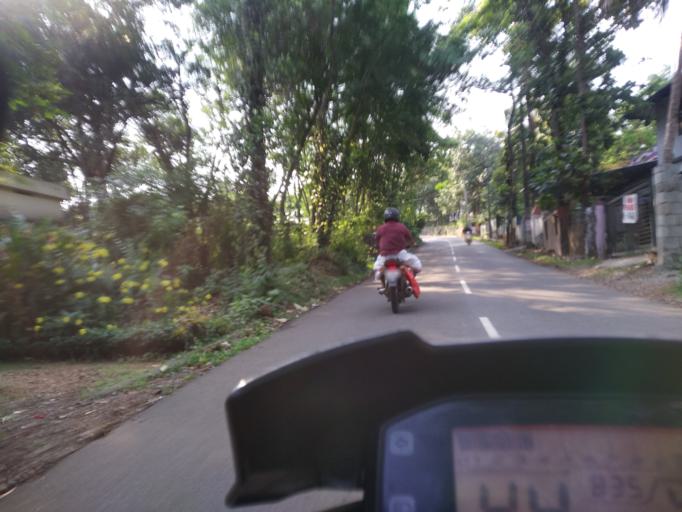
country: IN
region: Kerala
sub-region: Ernakulam
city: Ramamangalam
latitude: 9.9134
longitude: 76.4251
